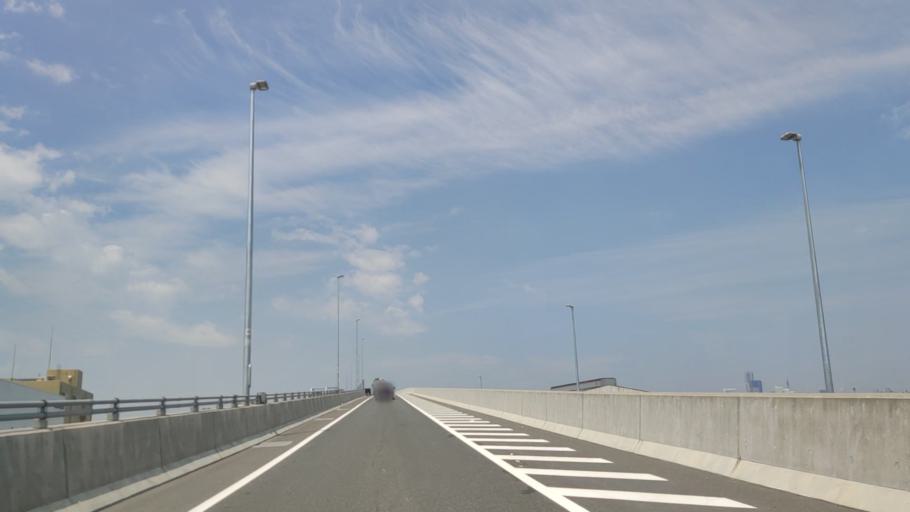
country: JP
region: Kanagawa
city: Yokohama
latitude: 35.4128
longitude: 139.6791
